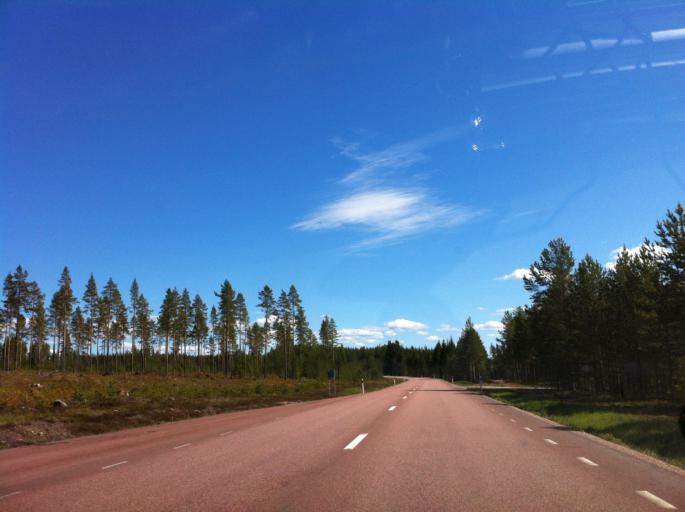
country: SE
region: Dalarna
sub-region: Mora Kommun
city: Mora
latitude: 60.9588
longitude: 14.7204
